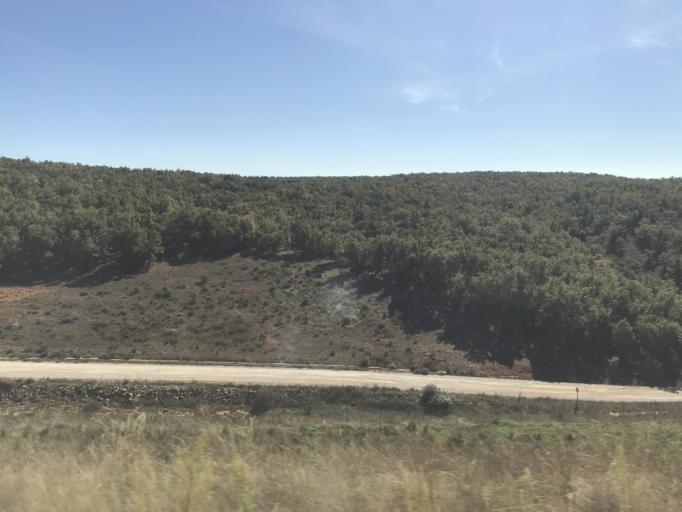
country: ES
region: Castille and Leon
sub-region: Provincia de Soria
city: Arcos de Jalon
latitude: 41.1341
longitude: -2.3299
